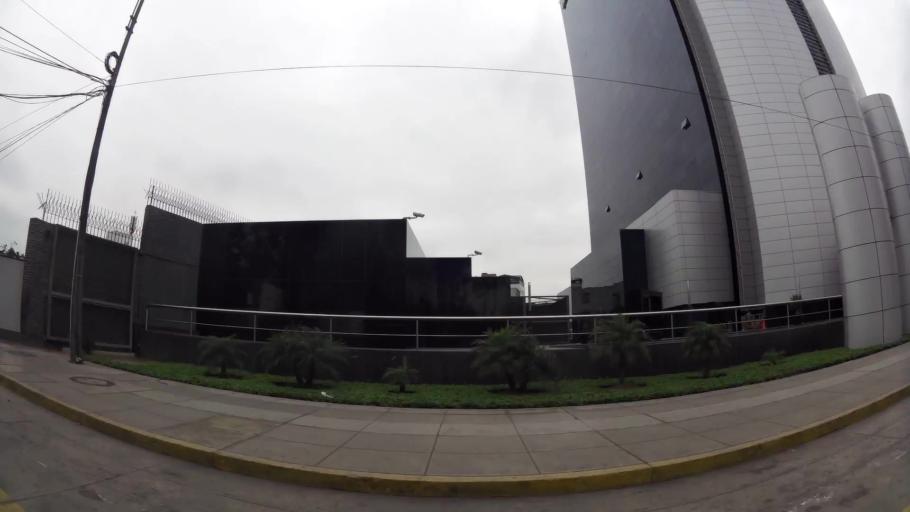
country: PE
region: Lima
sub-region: Lima
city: San Luis
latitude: -12.0934
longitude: -77.0217
